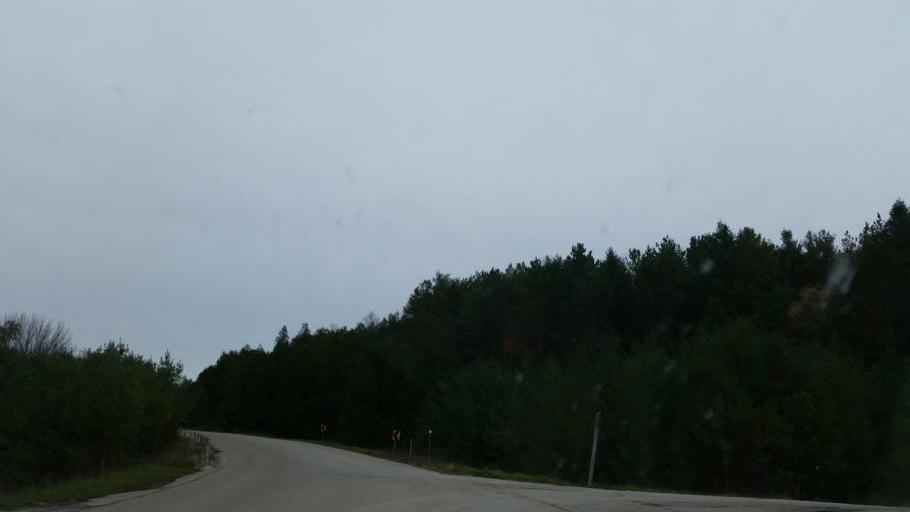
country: CA
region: Ontario
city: Wingham
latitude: 43.9753
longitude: -81.3329
